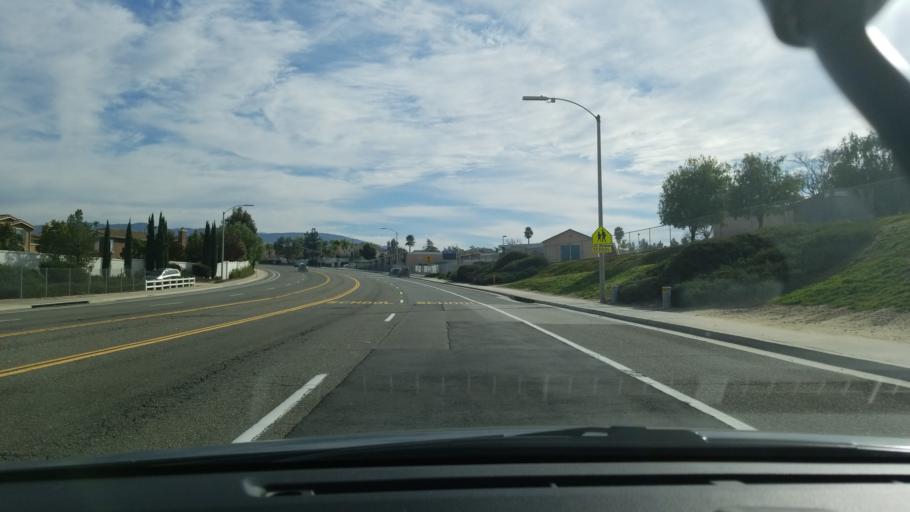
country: US
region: California
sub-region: Riverside County
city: Temecula
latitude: 33.4828
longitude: -117.0768
